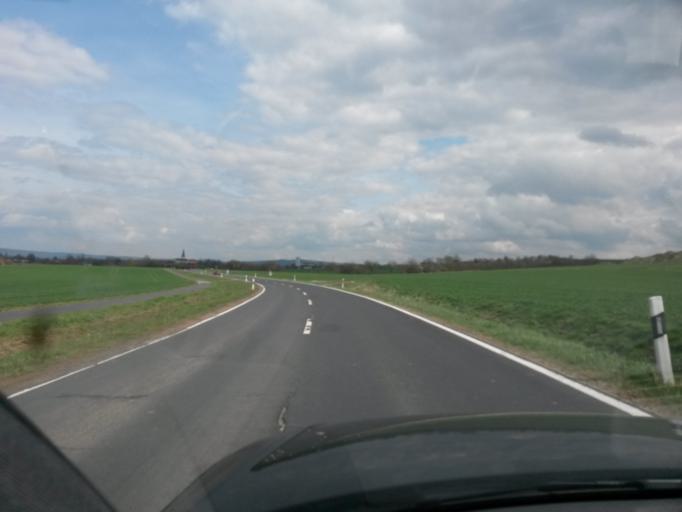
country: DE
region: Bavaria
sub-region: Regierungsbezirk Unterfranken
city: Frankenwinheim
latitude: 49.8839
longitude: 10.2968
